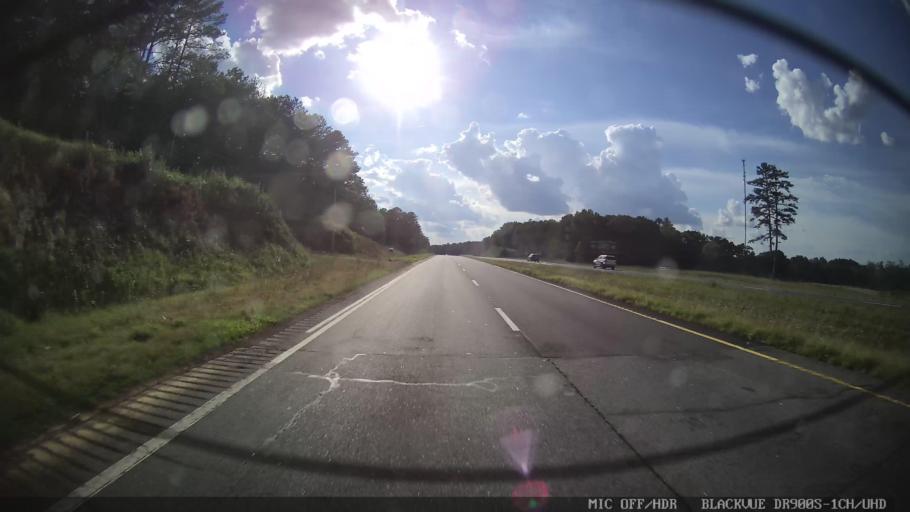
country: US
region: Georgia
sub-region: Bartow County
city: Euharlee
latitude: 34.2068
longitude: -85.0431
